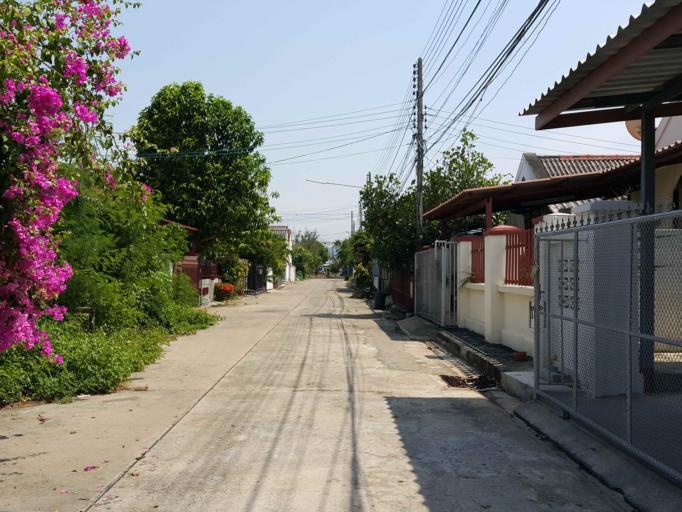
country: TH
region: Chiang Mai
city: Chiang Mai
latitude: 18.7501
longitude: 98.9597
